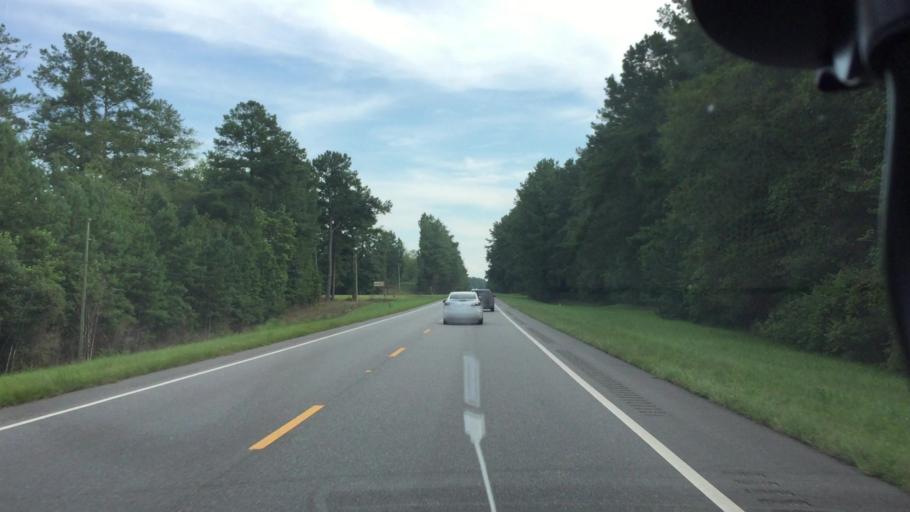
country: US
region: Alabama
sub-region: Coffee County
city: New Brockton
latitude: 31.5627
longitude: -85.9246
